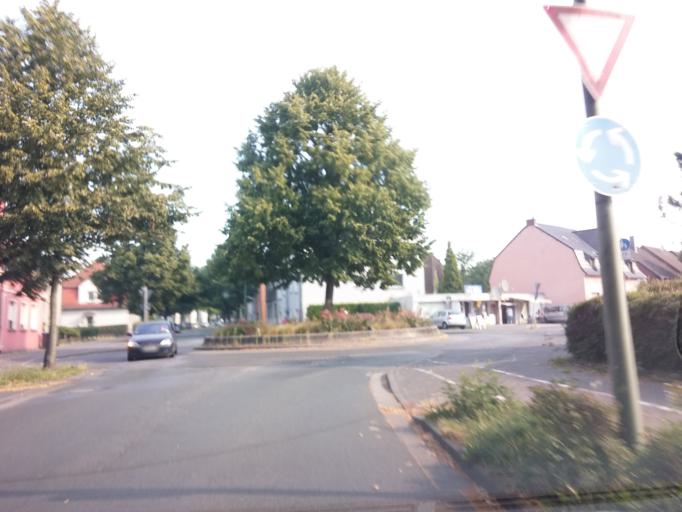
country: DE
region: North Rhine-Westphalia
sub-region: Regierungsbezirk Munster
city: Bottrop
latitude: 51.5250
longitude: 6.9753
